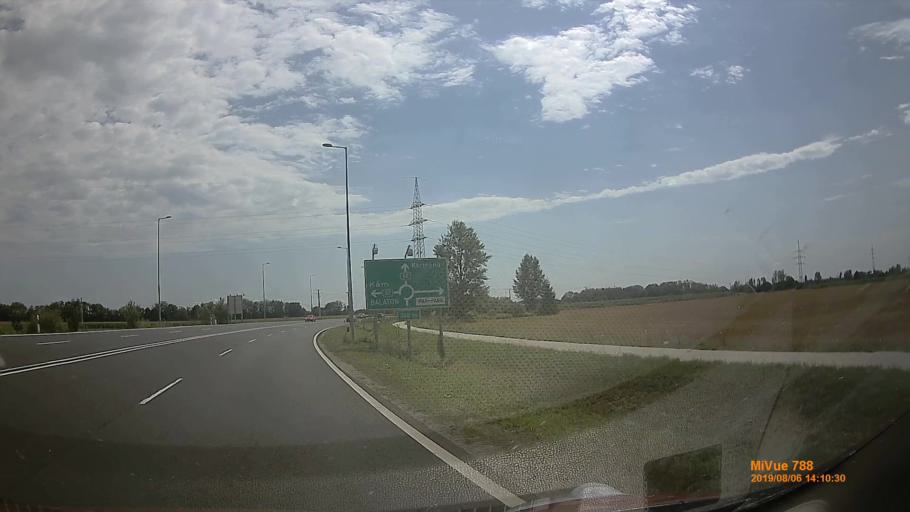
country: HU
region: Vas
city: Szombathely
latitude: 47.2237
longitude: 16.6583
